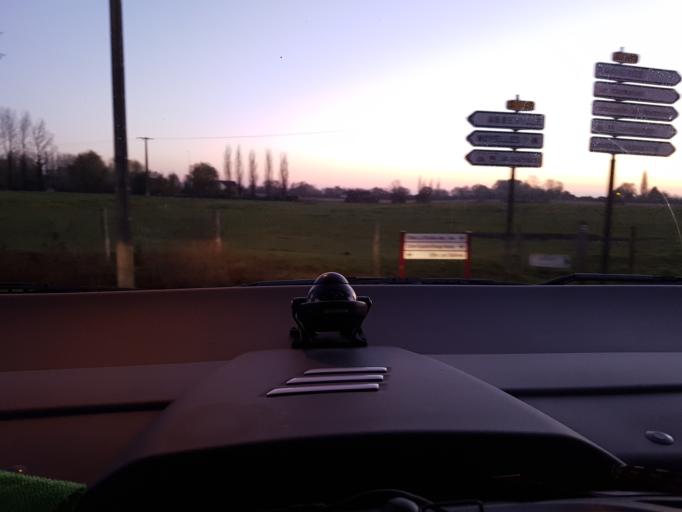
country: FR
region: Picardie
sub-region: Departement de la Somme
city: Saint-Valery-sur-Somme
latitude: 50.2105
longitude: 1.6899
